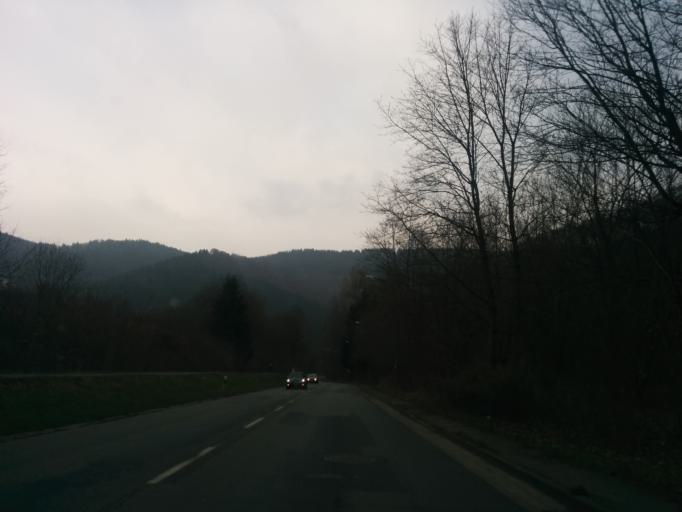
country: DE
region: Lower Saxony
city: Bad Lauterberg im Harz
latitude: 51.6384
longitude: 10.4847
